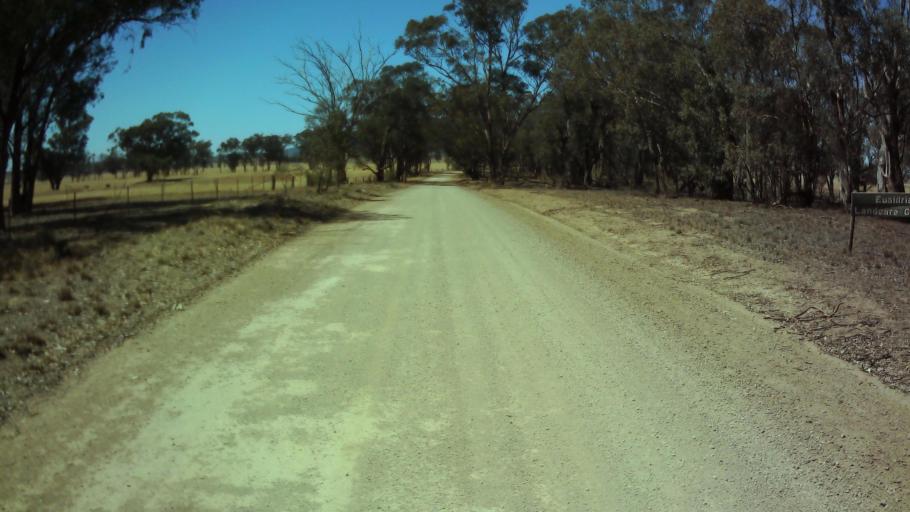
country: AU
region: New South Wales
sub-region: Weddin
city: Grenfell
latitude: -33.8865
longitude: 148.0877
